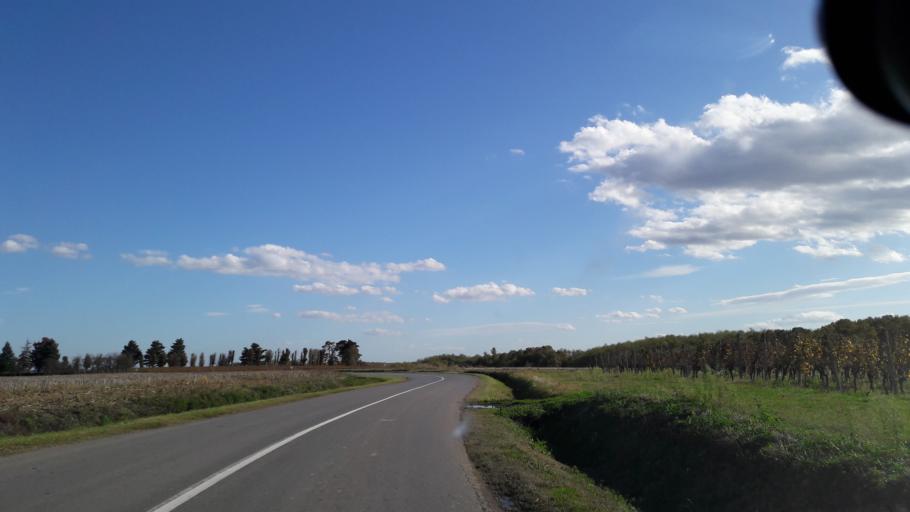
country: HR
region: Osjecko-Baranjska
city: Gorjani
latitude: 45.3811
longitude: 18.2593
